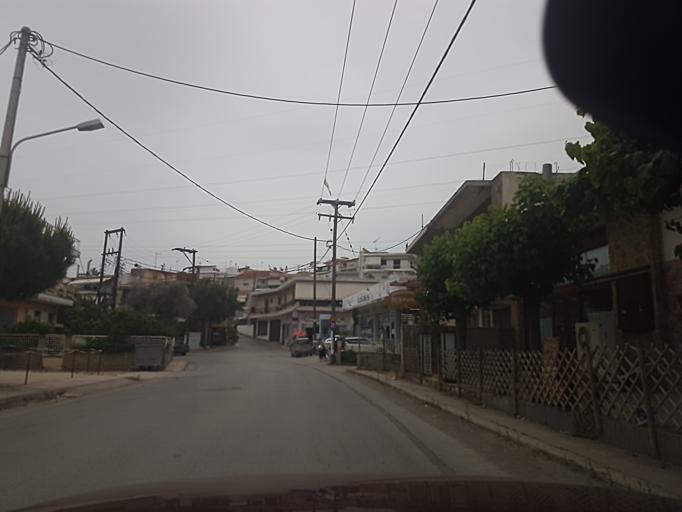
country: GR
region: Central Greece
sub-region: Nomos Evvoias
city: Chalkida
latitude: 38.4651
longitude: 23.6180
